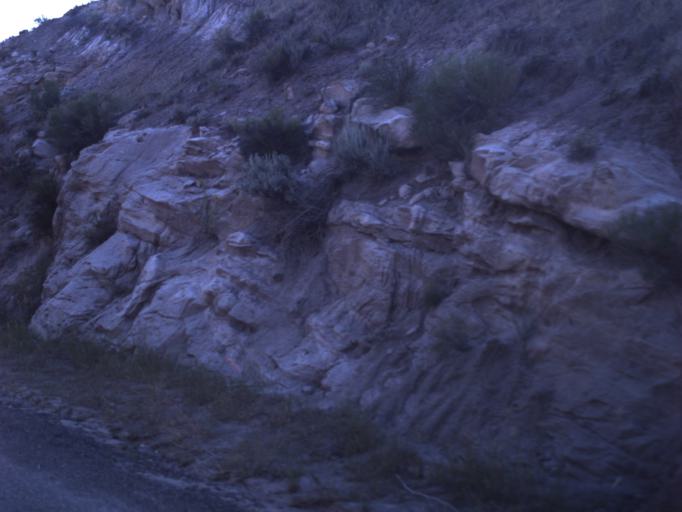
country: US
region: Utah
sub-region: Uintah County
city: Vernal
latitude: 40.5886
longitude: -109.4685
